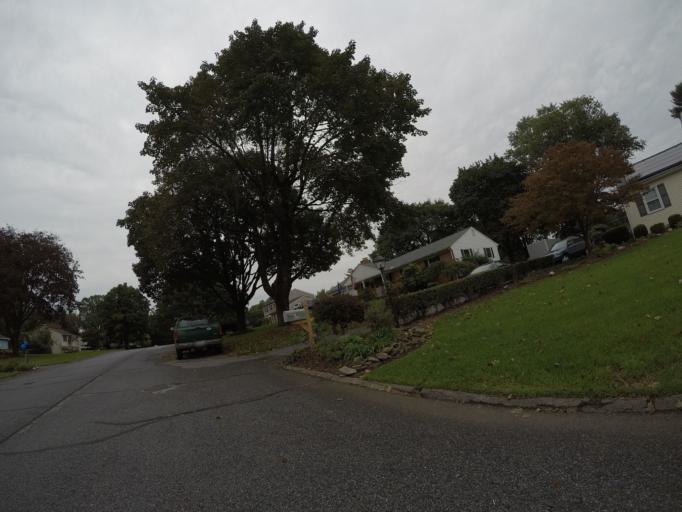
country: US
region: Maryland
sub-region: Howard County
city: Ellicott City
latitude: 39.2848
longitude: -76.8380
